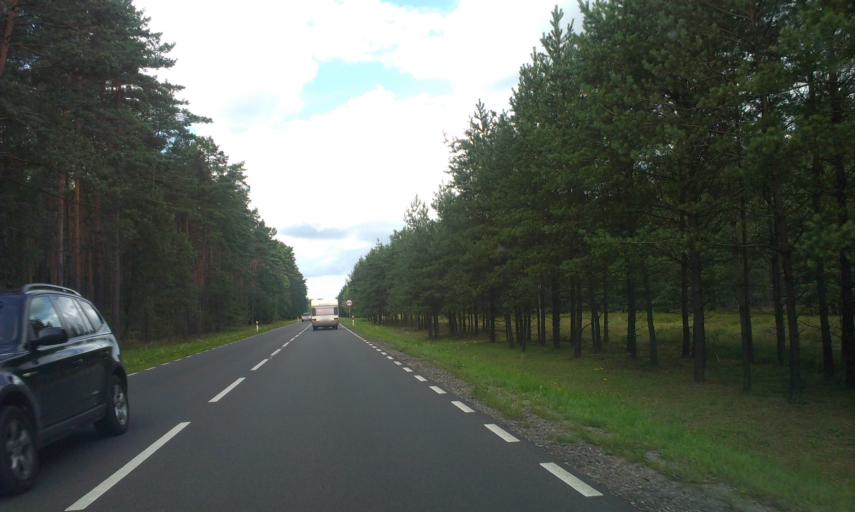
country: PL
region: West Pomeranian Voivodeship
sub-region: Powiat koszalinski
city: Sianow
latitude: 54.1014
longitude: 16.3481
